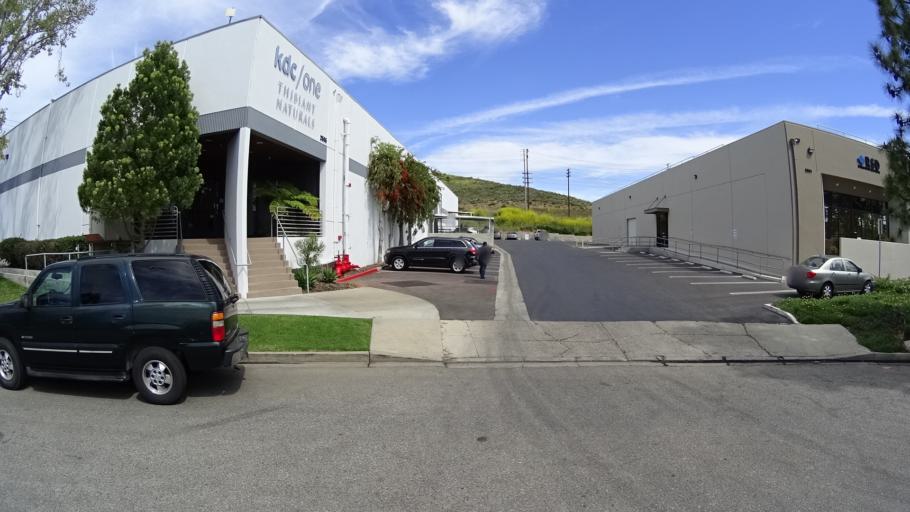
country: US
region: California
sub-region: Ventura County
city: Casa Conejo
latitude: 34.1946
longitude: -118.9326
